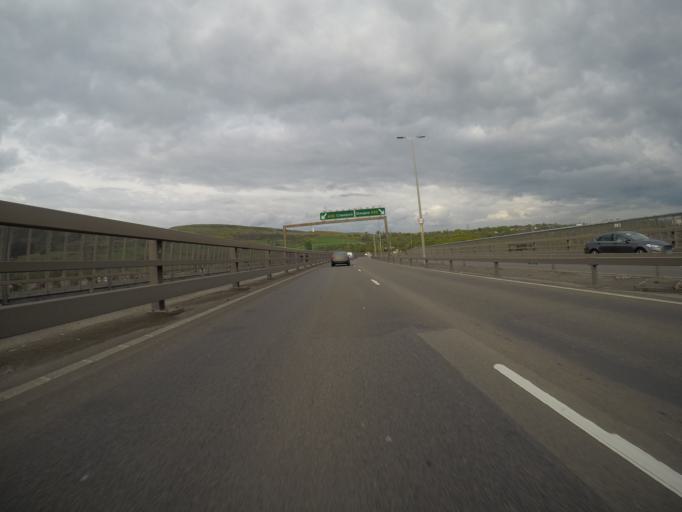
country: GB
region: Scotland
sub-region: West Dunbartonshire
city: Old Kilpatrick
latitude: 55.9227
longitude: -4.4563
